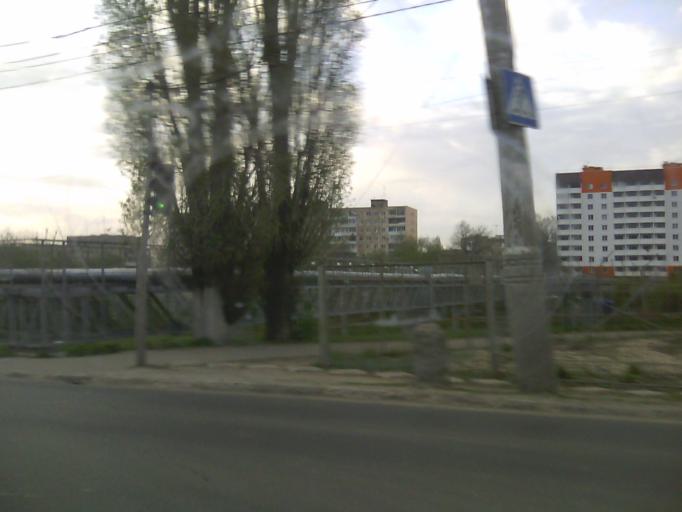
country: RU
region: Saratov
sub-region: Saratovskiy Rayon
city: Saratov
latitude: 51.5916
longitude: 45.9378
